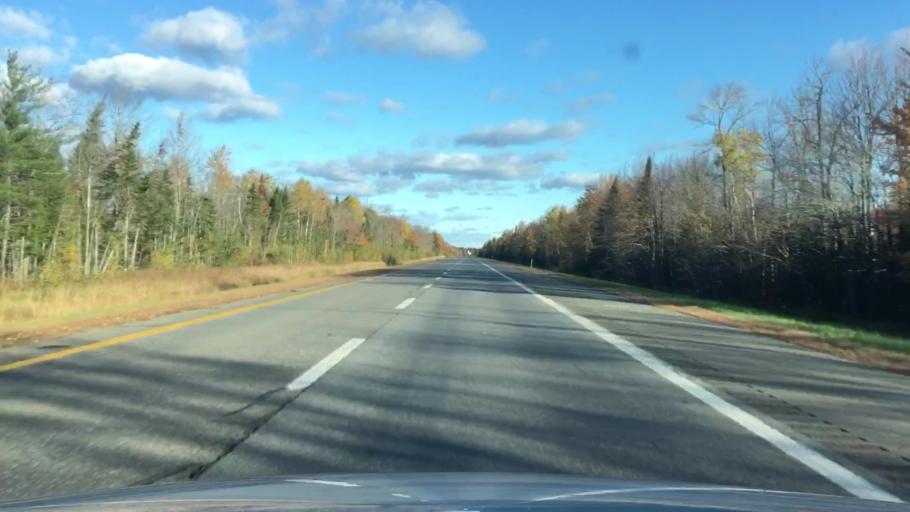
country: US
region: Maine
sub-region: Penobscot County
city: Greenbush
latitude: 45.0810
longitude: -68.6923
